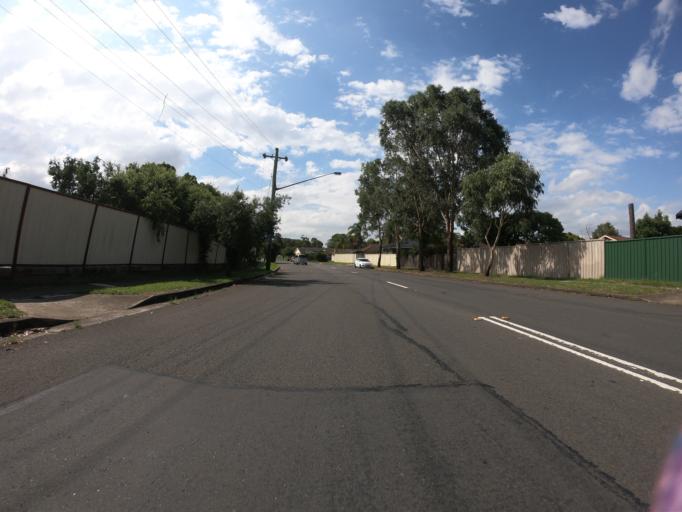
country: AU
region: New South Wales
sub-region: Blacktown
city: Blackett
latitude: -33.7433
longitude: 150.8284
